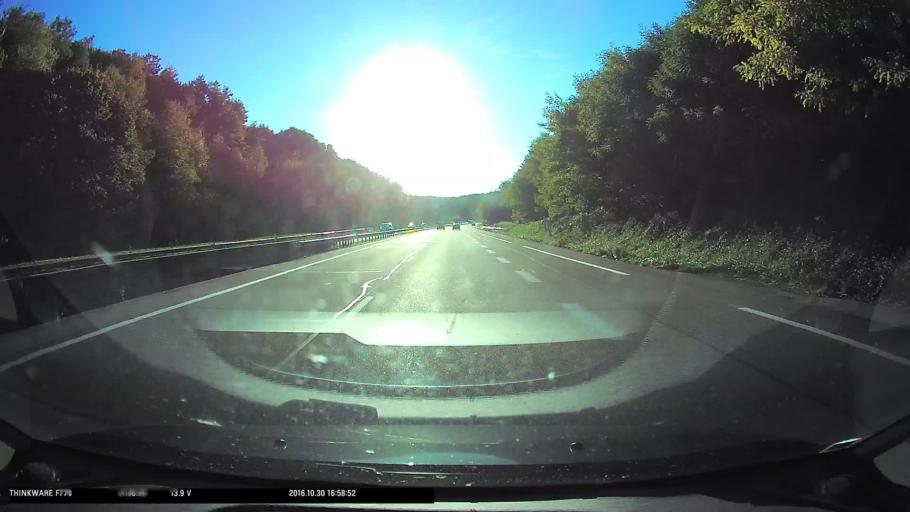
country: FR
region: Franche-Comte
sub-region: Departement du Jura
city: Dampierre
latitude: 47.1889
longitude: 5.7479
